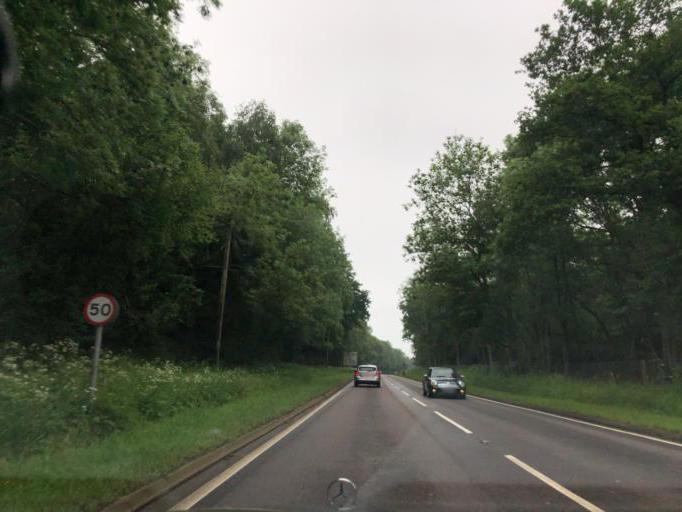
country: GB
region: England
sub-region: Warwickshire
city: Wellesbourne Mountford
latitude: 52.2298
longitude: -1.5428
